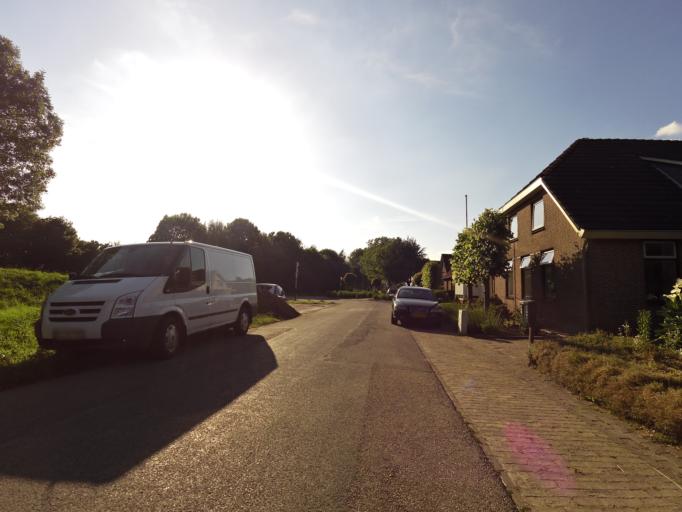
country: NL
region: Gelderland
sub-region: Gemeente Zevenaar
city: Zevenaar
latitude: 51.8838
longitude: 6.0717
